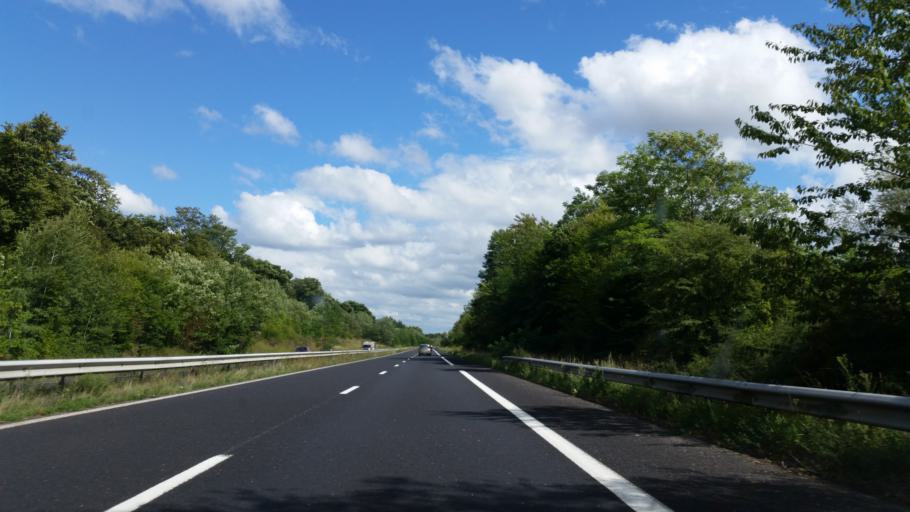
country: FR
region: Lorraine
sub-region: Departement de Meurthe-et-Moselle
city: Flavigny-sur-Moselle
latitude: 48.5342
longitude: 6.2130
